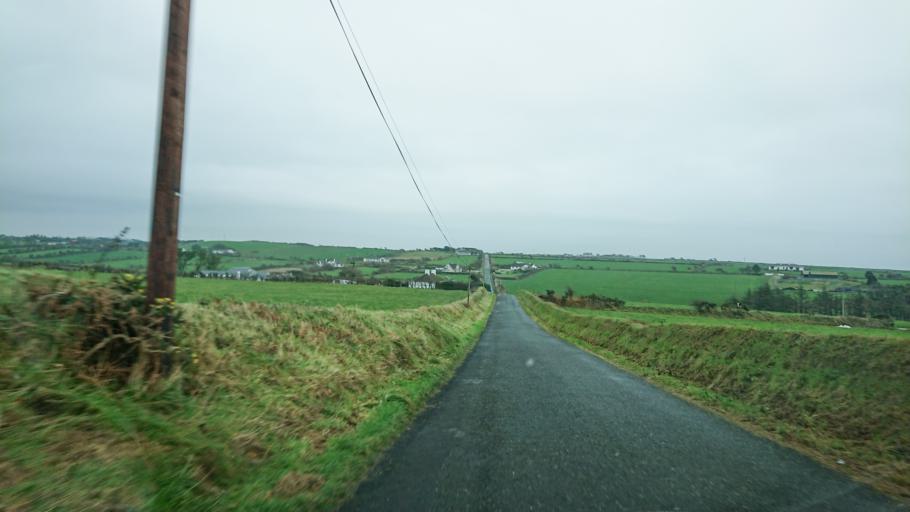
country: IE
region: Munster
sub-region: Waterford
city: Tra Mhor
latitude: 52.1431
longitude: -7.2019
